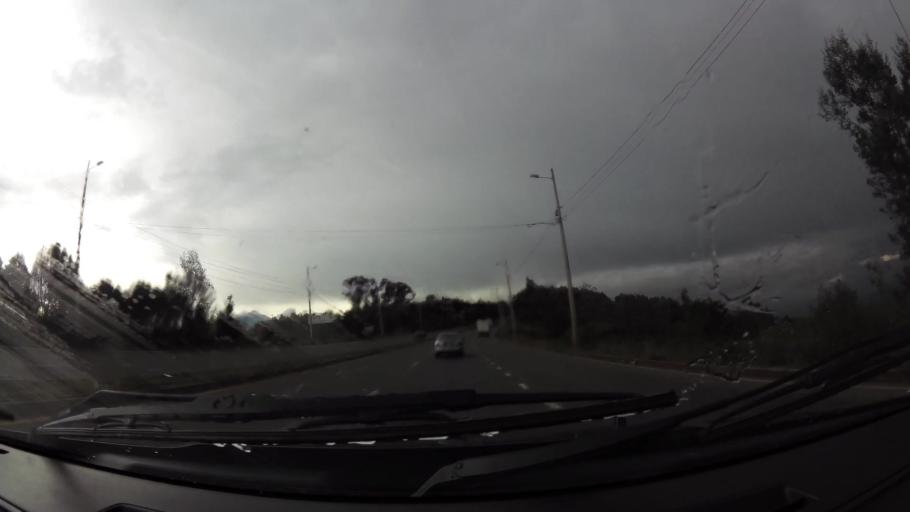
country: EC
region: Pichincha
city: Sangolqui
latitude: -0.3131
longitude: -78.5223
